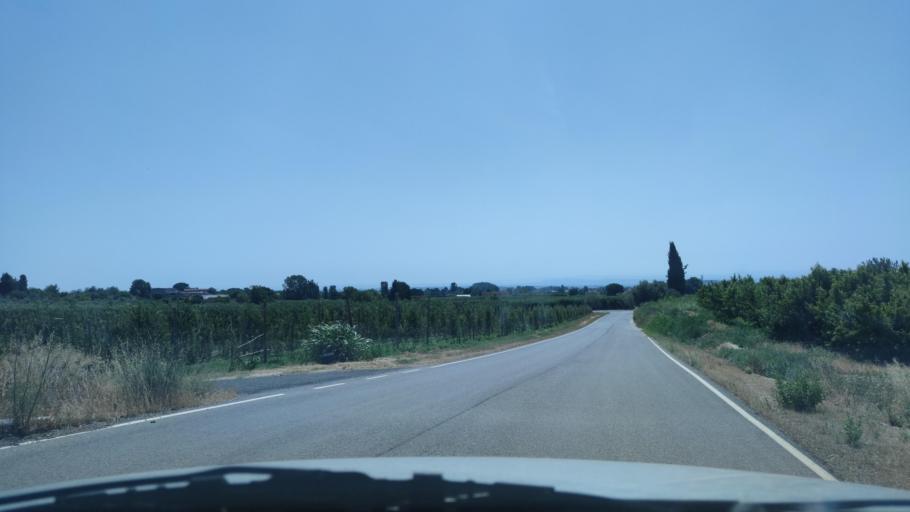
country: ES
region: Catalonia
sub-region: Provincia de Lleida
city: Torrefarrera
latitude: 41.6581
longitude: 0.5891
